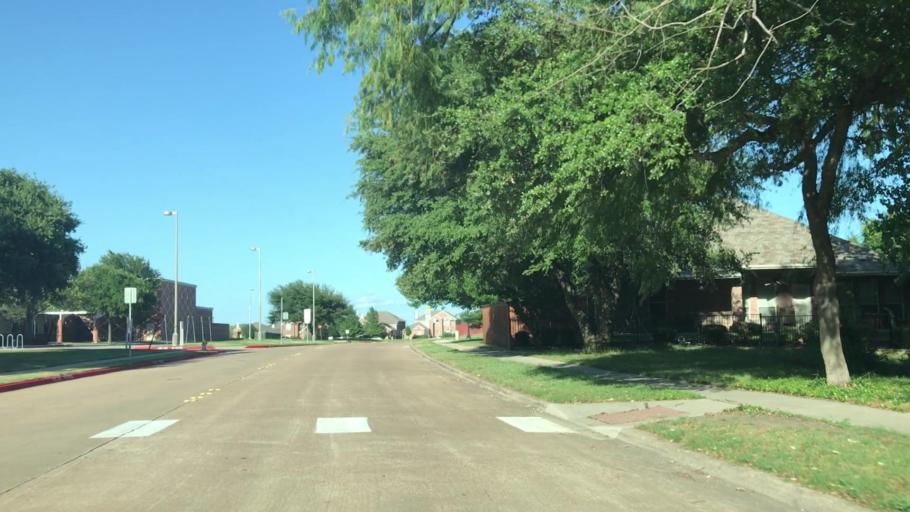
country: US
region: Texas
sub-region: Collin County
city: Frisco
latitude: 33.1233
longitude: -96.7714
